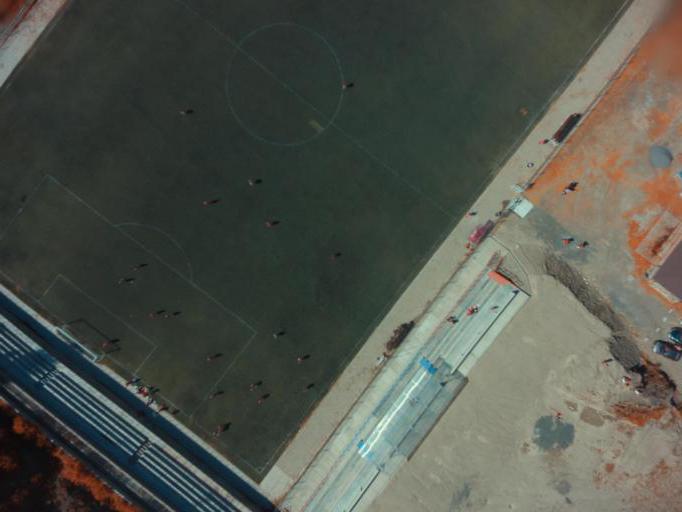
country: BO
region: La Paz
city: La Paz
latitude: -16.5353
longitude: -68.0664
